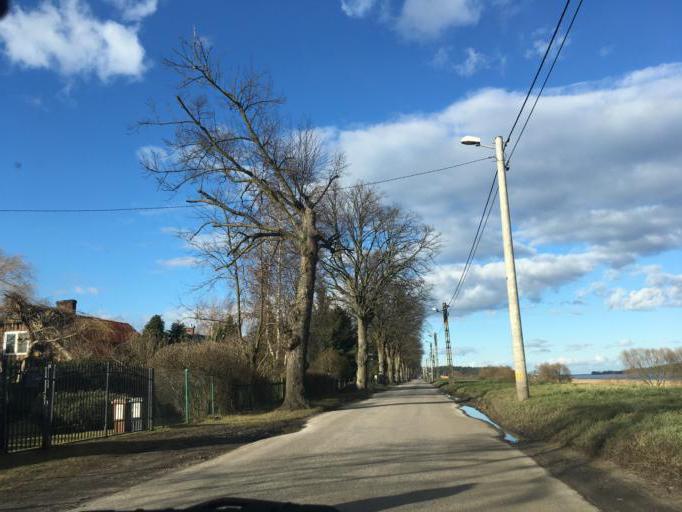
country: PL
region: Pomeranian Voivodeship
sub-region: Powiat nowodworski
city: Ostaszewo
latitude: 54.3242
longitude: 18.9321
